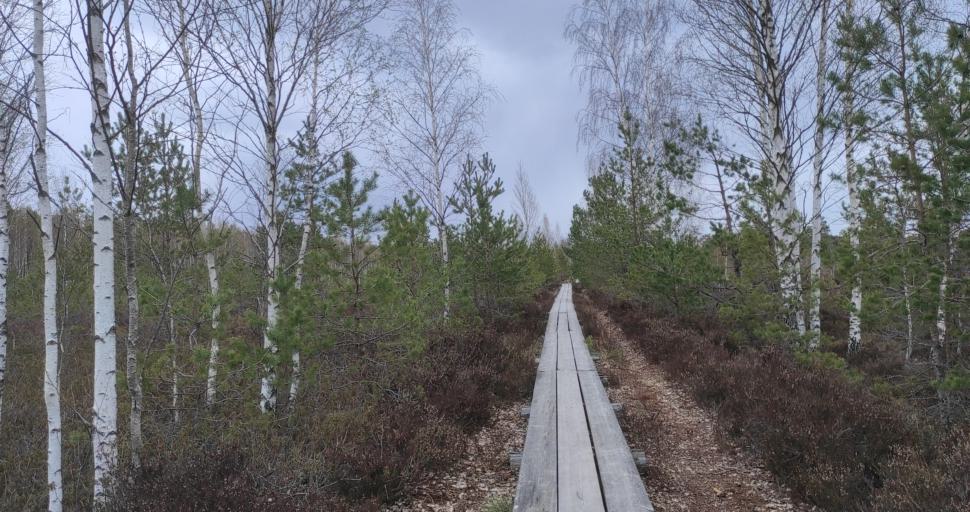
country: LV
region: Dundaga
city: Dundaga
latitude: 57.3543
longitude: 22.1525
